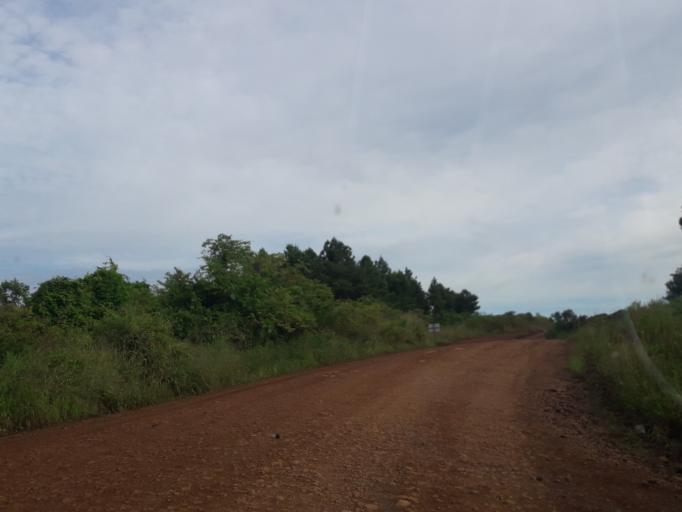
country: AR
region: Misiones
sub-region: Departamento de San Pedro
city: San Pedro
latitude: -26.5367
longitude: -53.9406
